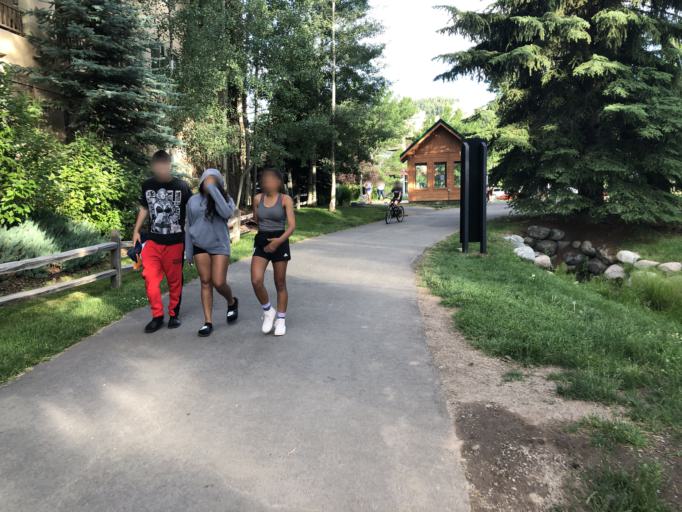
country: US
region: Colorado
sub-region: Eagle County
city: Avon
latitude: 39.6368
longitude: -106.5272
